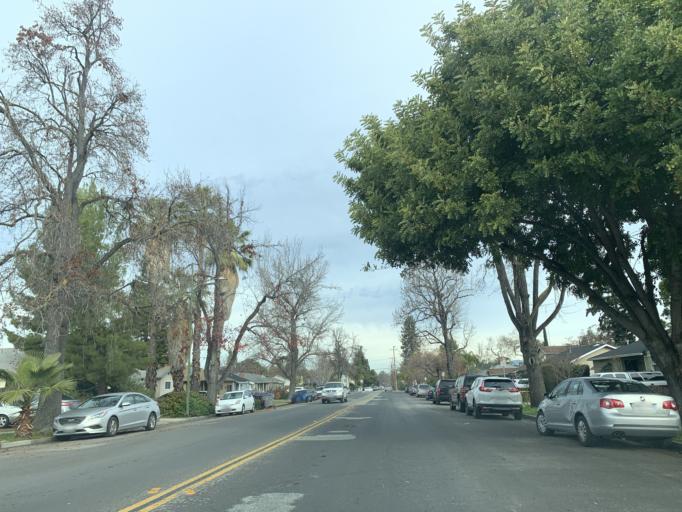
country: US
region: California
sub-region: Santa Clara County
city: Buena Vista
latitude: 37.3182
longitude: -121.9238
